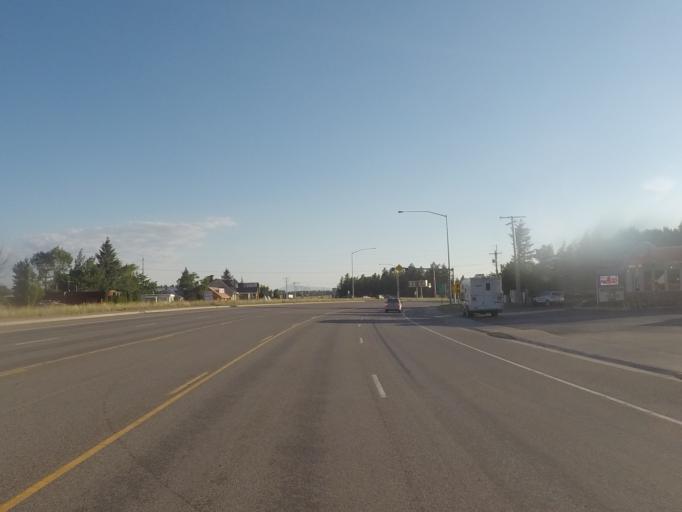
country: US
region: Montana
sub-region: Flathead County
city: Columbia Falls
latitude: 48.3649
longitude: -114.1470
